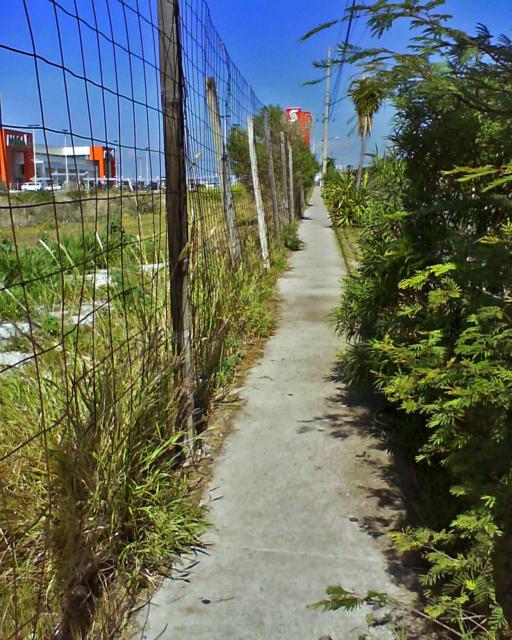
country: MX
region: Queretaro
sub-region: Queretaro
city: Sergio Villasenor
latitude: 20.6417
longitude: -100.4115
